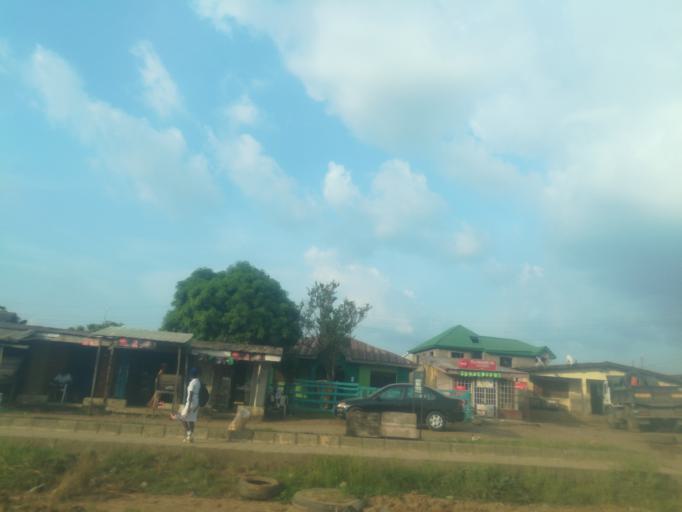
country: NG
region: Ogun
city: Abeokuta
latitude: 7.1683
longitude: 3.2988
